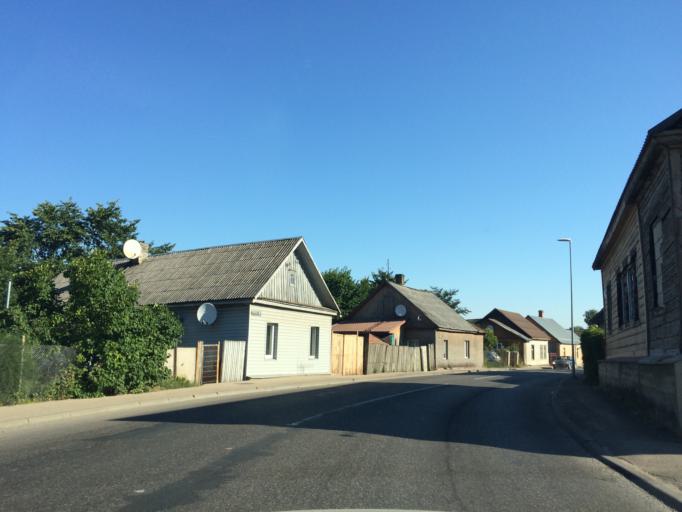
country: LV
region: Rezekne
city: Rezekne
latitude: 56.5010
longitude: 27.3411
